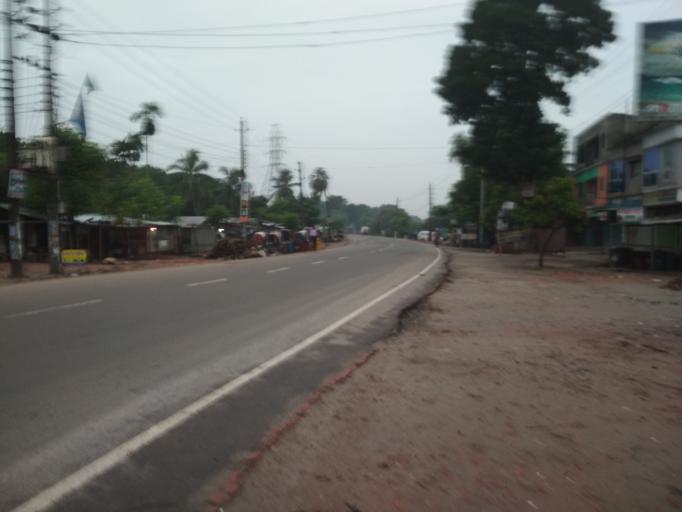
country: BD
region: Khulna
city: Jessore
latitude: 23.1823
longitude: 89.1903
